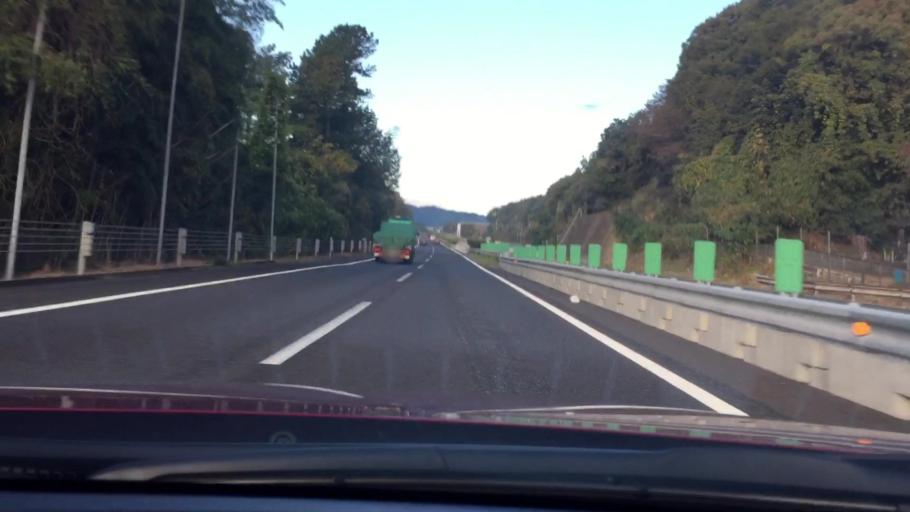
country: JP
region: Hyogo
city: Yamazakicho-nakabirose
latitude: 34.9902
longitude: 134.5891
